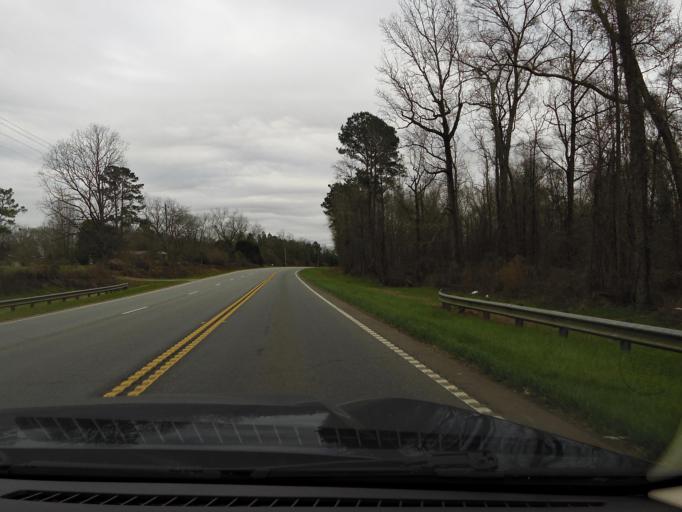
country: US
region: Georgia
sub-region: Randolph County
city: Cuthbert
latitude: 31.7783
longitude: -84.7307
